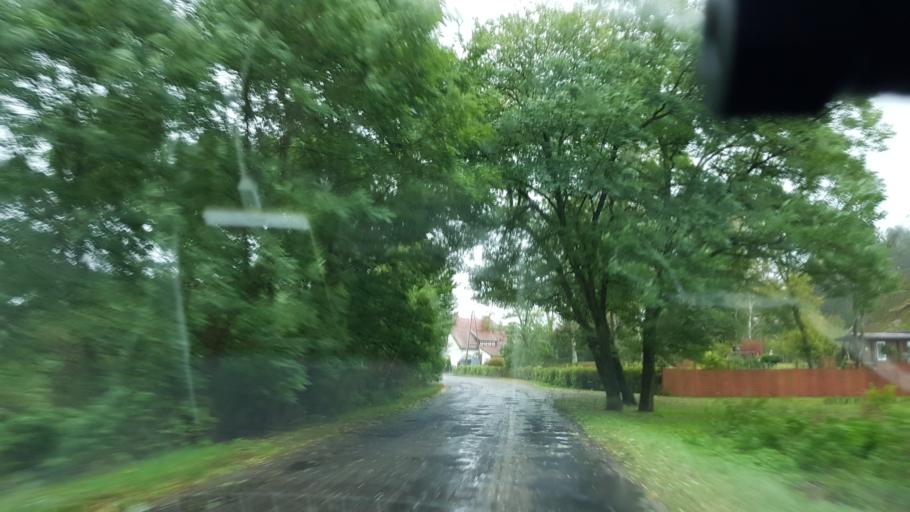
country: PL
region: West Pomeranian Voivodeship
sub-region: Powiat goleniowski
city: Stepnica
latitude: 53.6808
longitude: 14.7154
